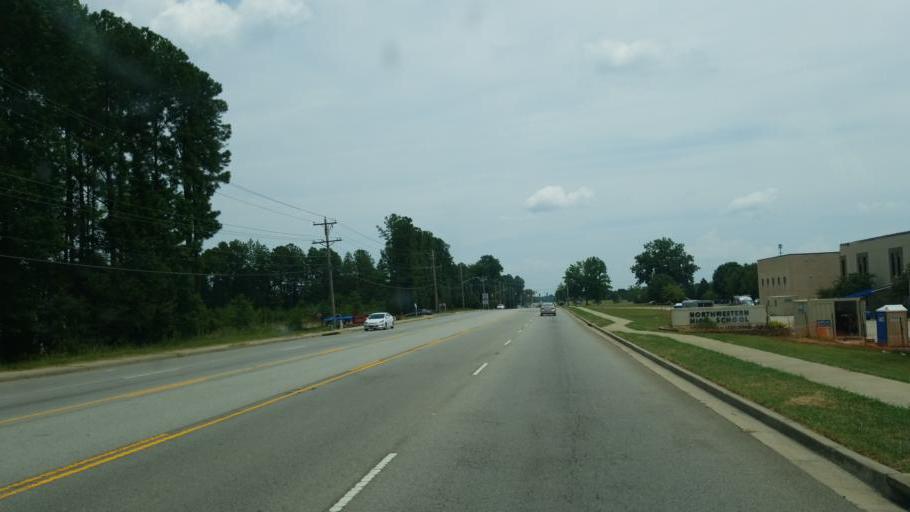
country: US
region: South Carolina
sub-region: York County
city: Newport
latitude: 34.9508
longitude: -81.0834
